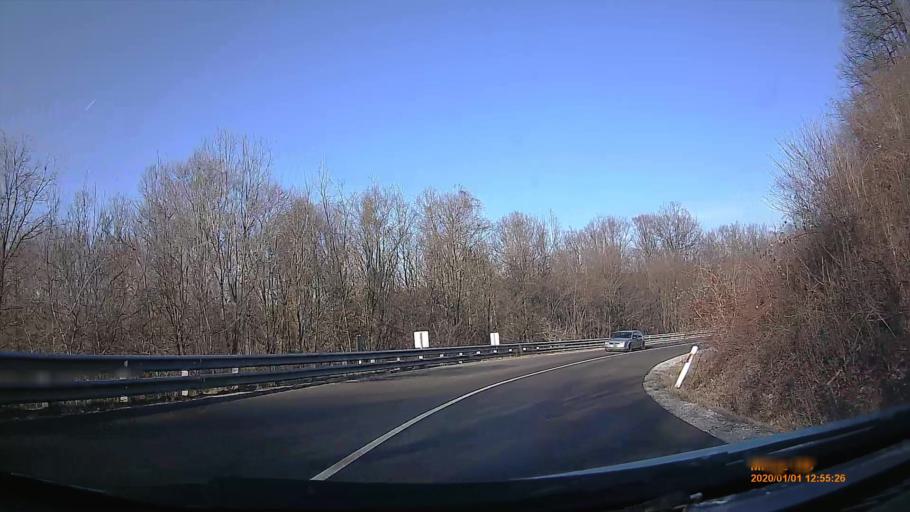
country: HU
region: Heves
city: Paradsasvar
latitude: 47.9114
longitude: 19.9895
